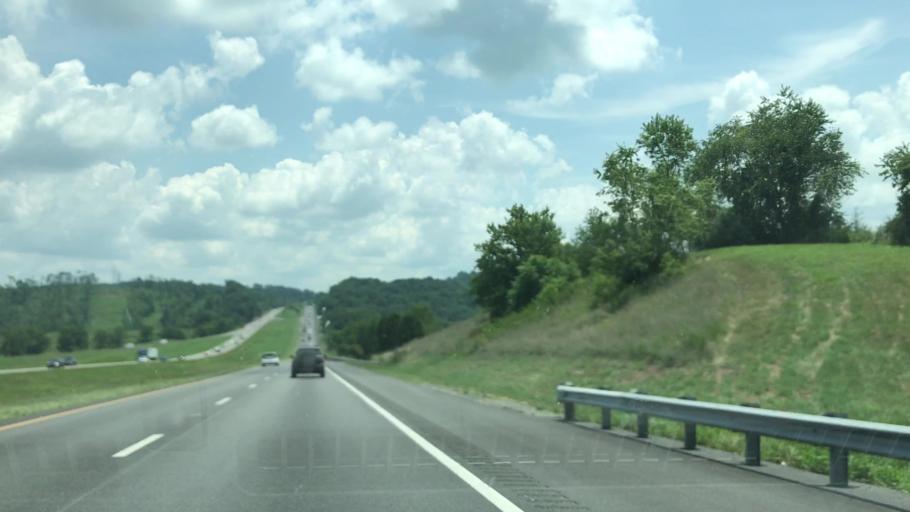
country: US
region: Virginia
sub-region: Pulaski County
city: Pulaski
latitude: 36.9133
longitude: -80.8919
